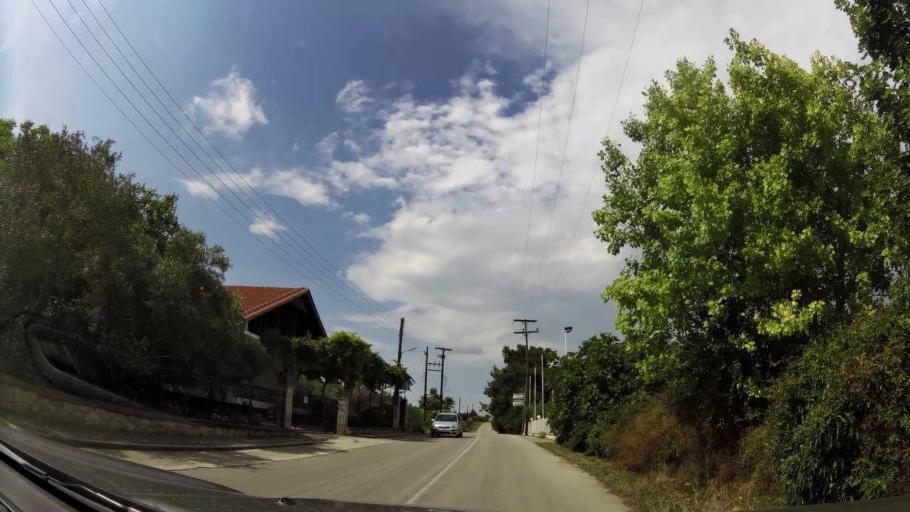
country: GR
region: Central Macedonia
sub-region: Nomos Pierias
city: Makrygialos
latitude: 40.3958
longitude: 22.6166
